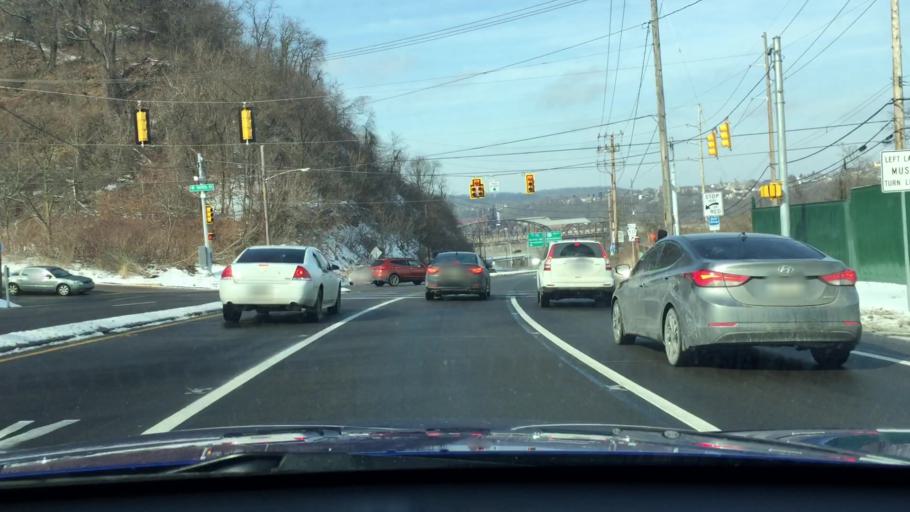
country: US
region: Pennsylvania
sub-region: Allegheny County
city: Whitaker
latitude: 40.4011
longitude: -79.8803
